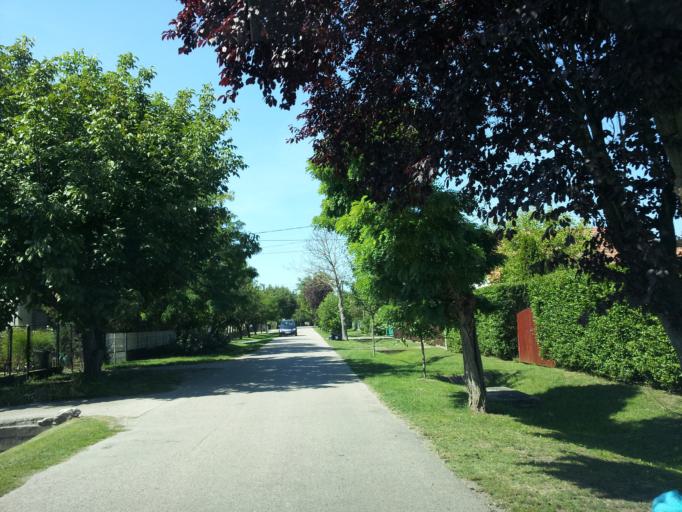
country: HU
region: Somogy
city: Zamardi
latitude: 46.8798
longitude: 17.9358
